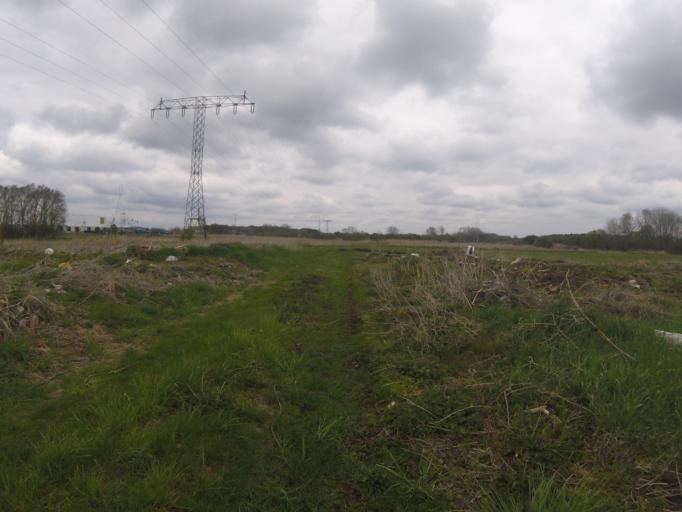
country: DE
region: Brandenburg
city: Mittenwalde
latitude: 52.2575
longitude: 13.5742
